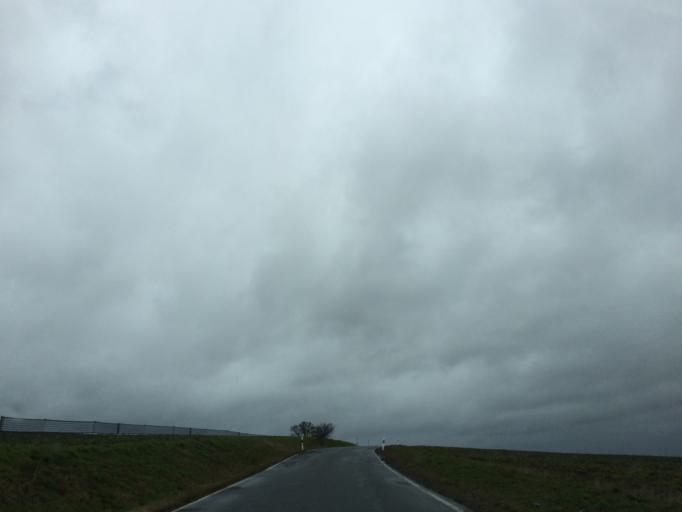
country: DE
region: Thuringia
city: Quaschwitz
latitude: 50.6762
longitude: 11.7090
